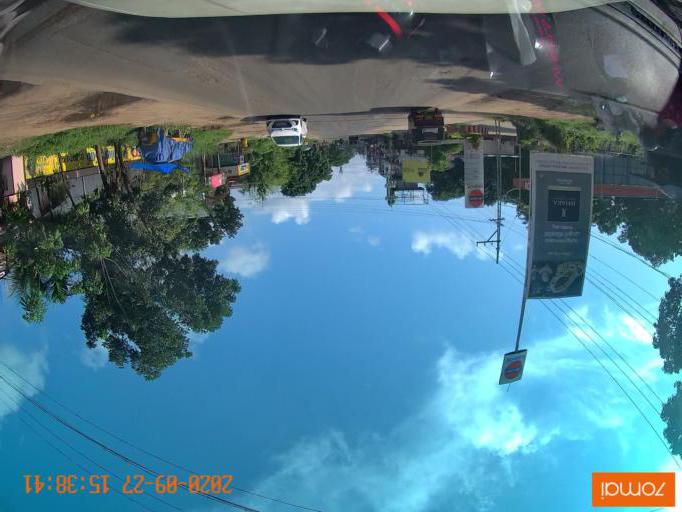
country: IN
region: Kerala
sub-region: Thrissur District
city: Thanniyam
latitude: 10.4639
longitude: 76.0832
